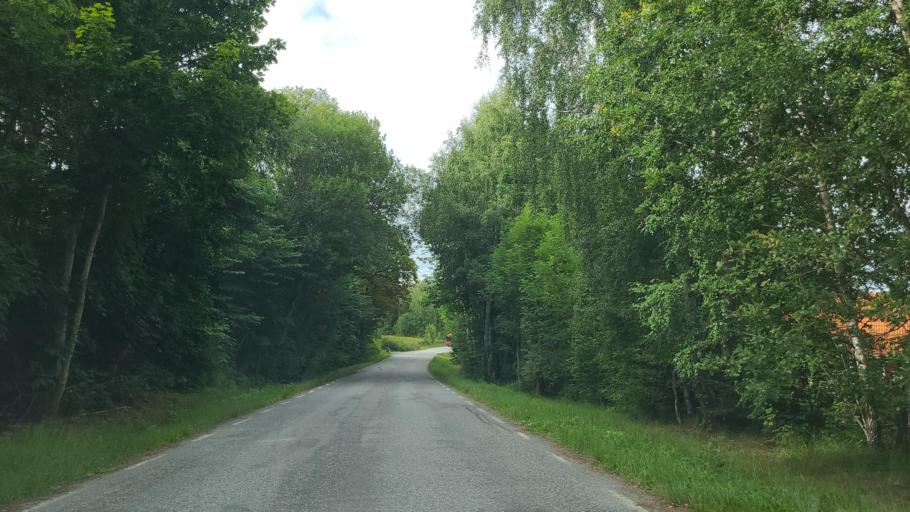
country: SE
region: Stockholm
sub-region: Upplands-Bro Kommun
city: Bro
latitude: 59.4892
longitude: 17.5672
